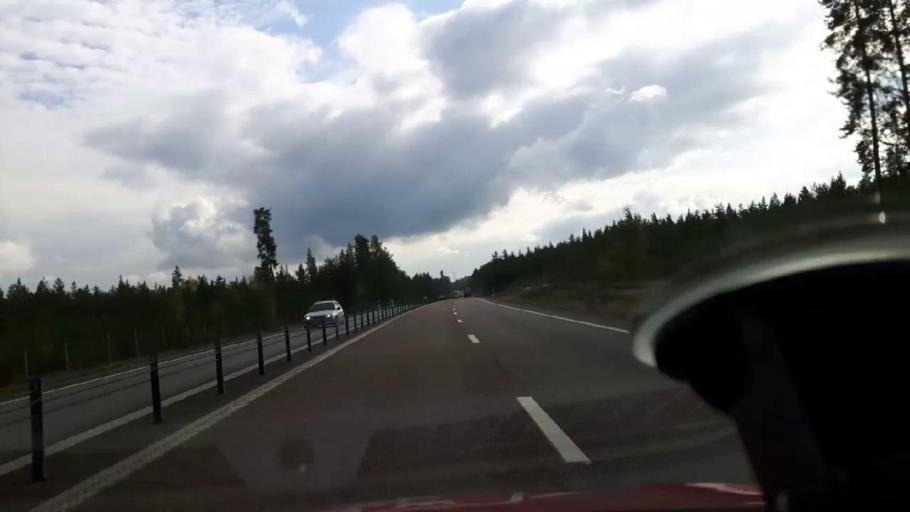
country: SE
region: Gaevleborg
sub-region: Gavle Kommun
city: Norrsundet
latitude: 60.9808
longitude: 17.0172
